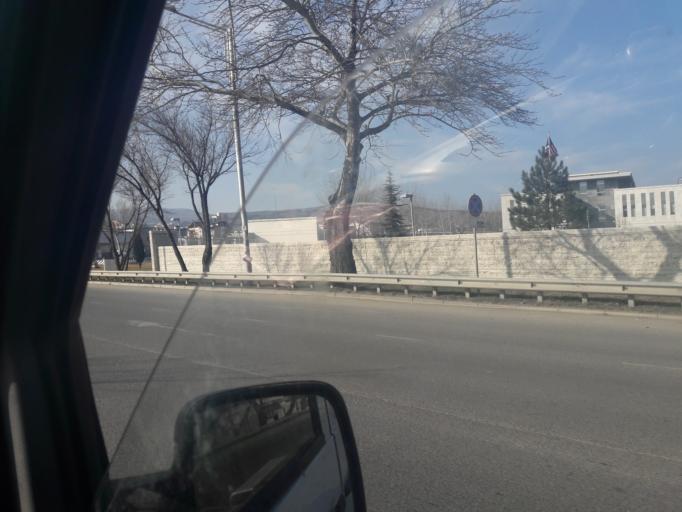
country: GE
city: Zahesi
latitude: 41.7875
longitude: 44.7759
